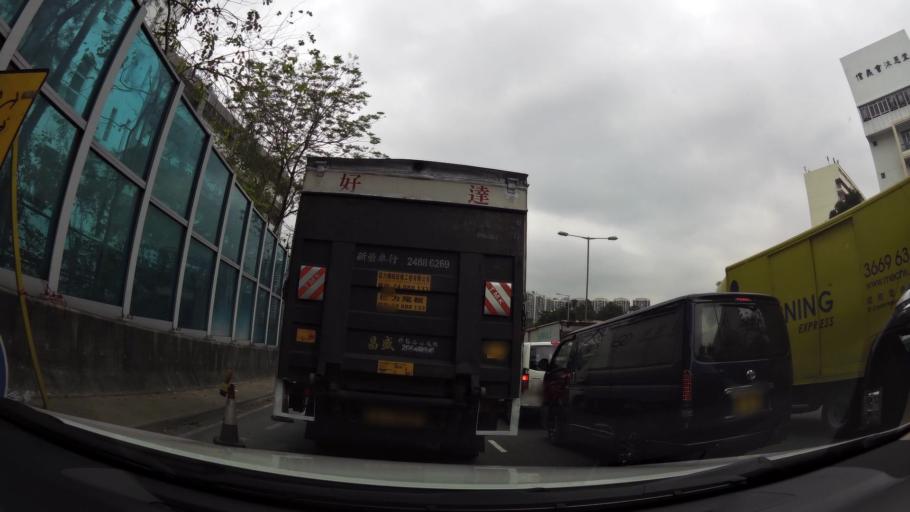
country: HK
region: Sha Tin
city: Sha Tin
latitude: 22.3899
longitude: 114.1978
